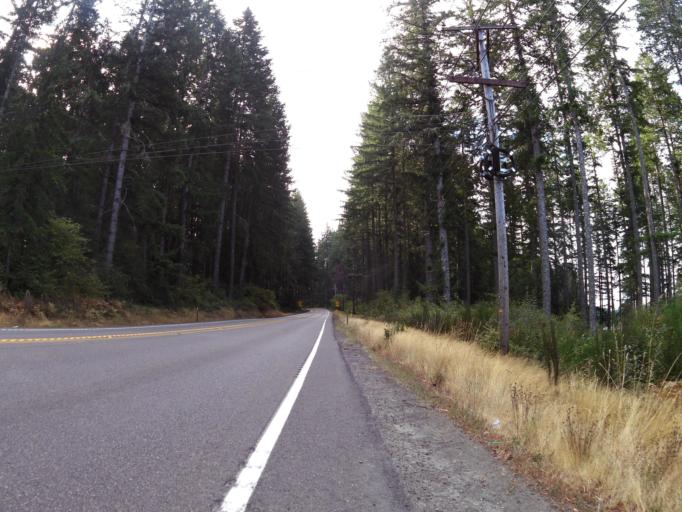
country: US
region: Washington
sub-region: Mason County
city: Allyn
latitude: 47.4149
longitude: -122.8453
